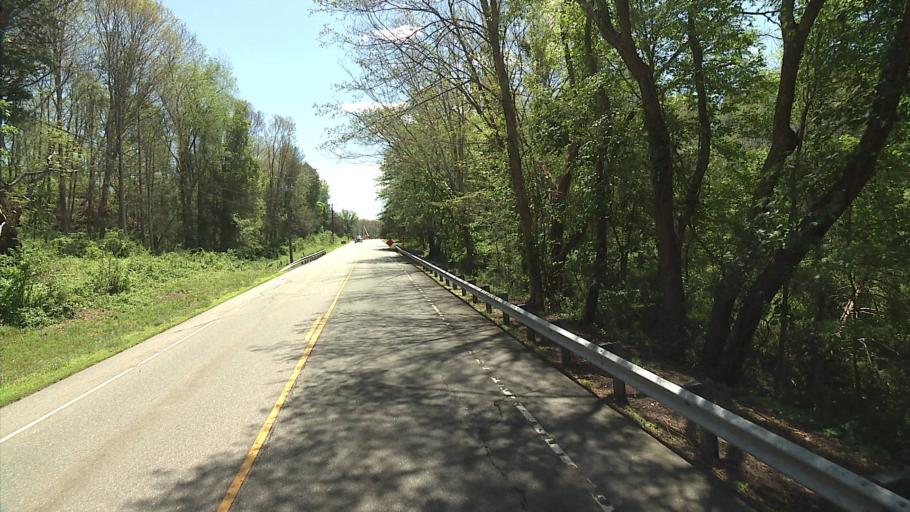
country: US
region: Connecticut
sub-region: Middlesex County
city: Moodus
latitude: 41.4991
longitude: -72.4673
